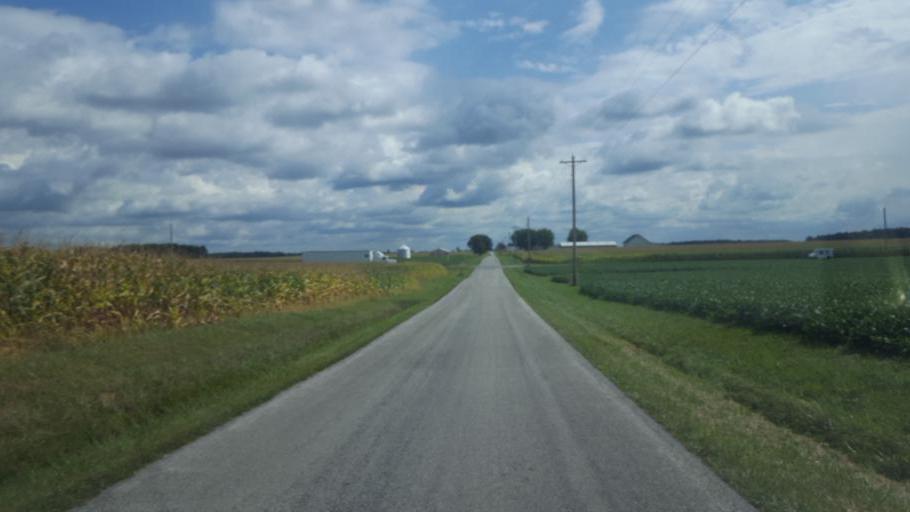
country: US
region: Ohio
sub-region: Sandusky County
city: Green Springs
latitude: 41.0957
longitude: -82.9978
